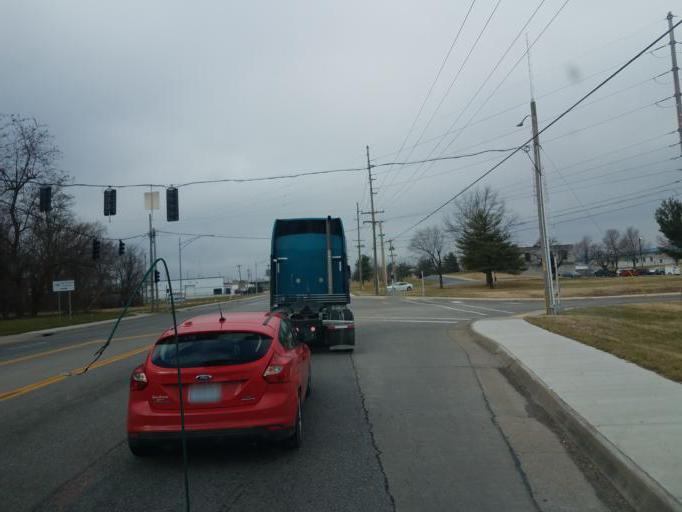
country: US
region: Missouri
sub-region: Greene County
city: Springfield
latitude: 37.2391
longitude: -93.2288
